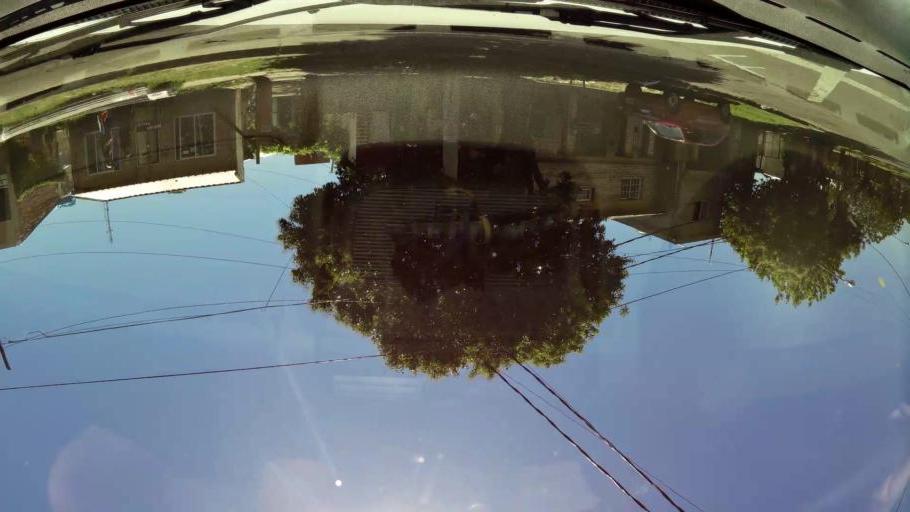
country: AR
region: Buenos Aires
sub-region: Partido de General San Martin
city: General San Martin
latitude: -34.5171
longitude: -58.5551
